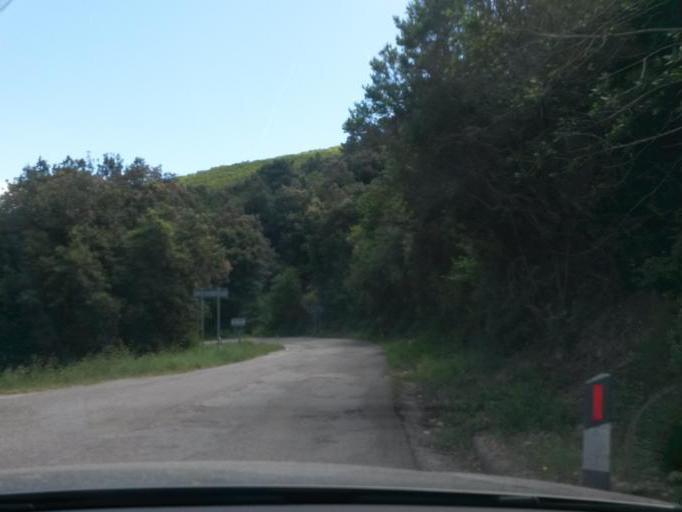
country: IT
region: Tuscany
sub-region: Provincia di Livorno
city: Campo nell'Elba
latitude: 42.7596
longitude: 10.2748
